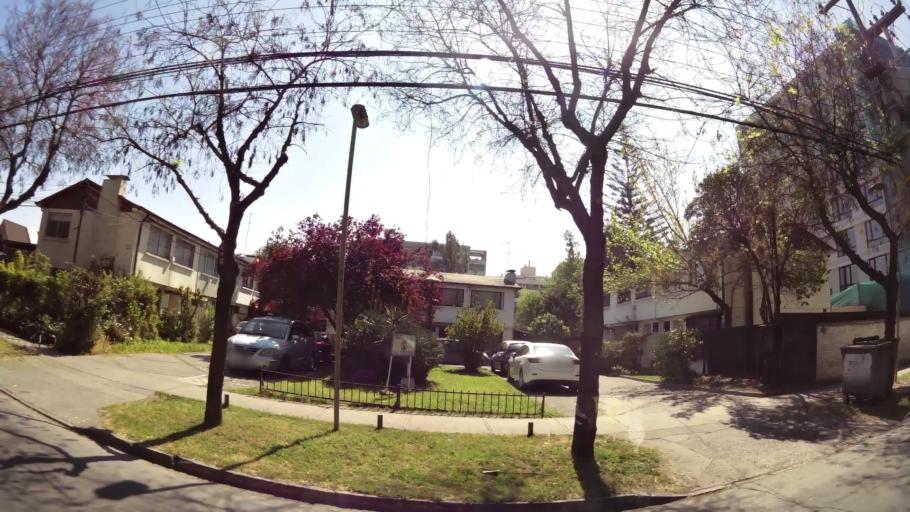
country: CL
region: Santiago Metropolitan
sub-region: Provincia de Santiago
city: Villa Presidente Frei, Nunoa, Santiago, Chile
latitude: -33.4291
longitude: -70.5768
